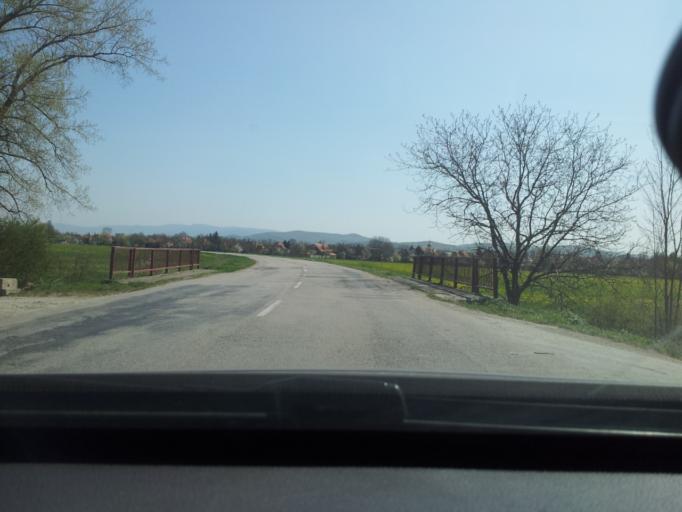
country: SK
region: Nitriansky
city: Banovce nad Bebravou
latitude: 48.6134
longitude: 18.2598
